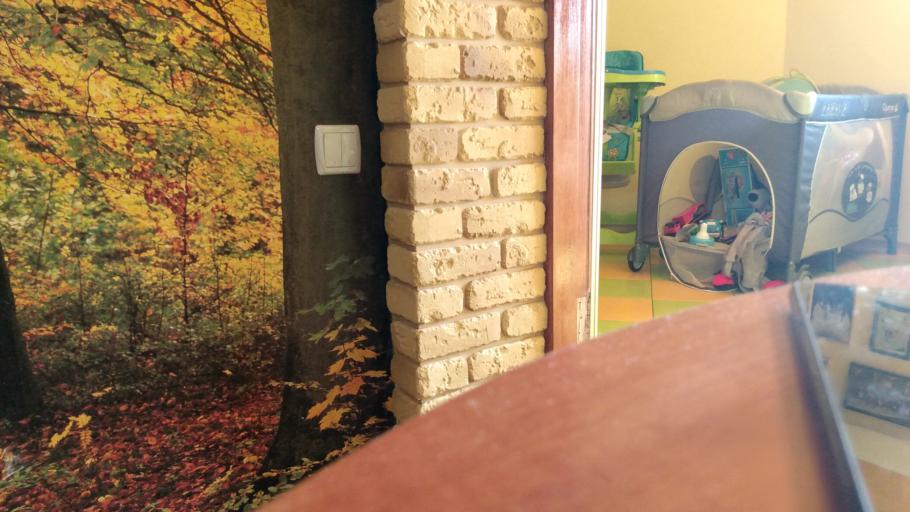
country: RU
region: Tverskaya
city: Vasil'yevskiy Mokh
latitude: 57.0299
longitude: 35.8255
